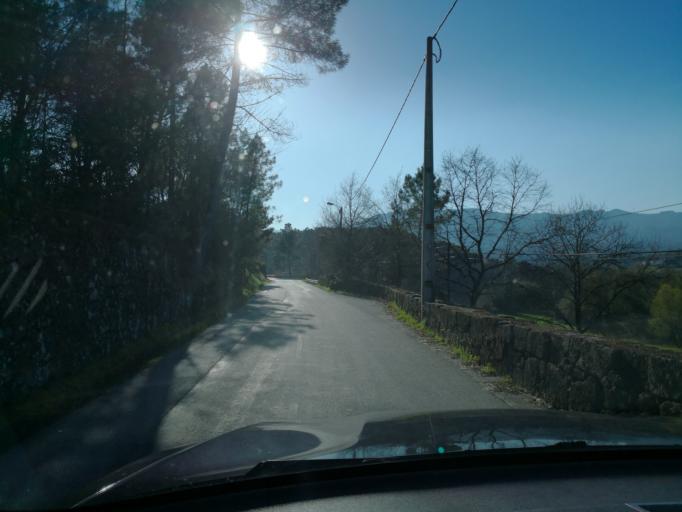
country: PT
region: Vila Real
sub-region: Vila Real
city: Vila Real
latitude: 41.2936
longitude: -7.7702
